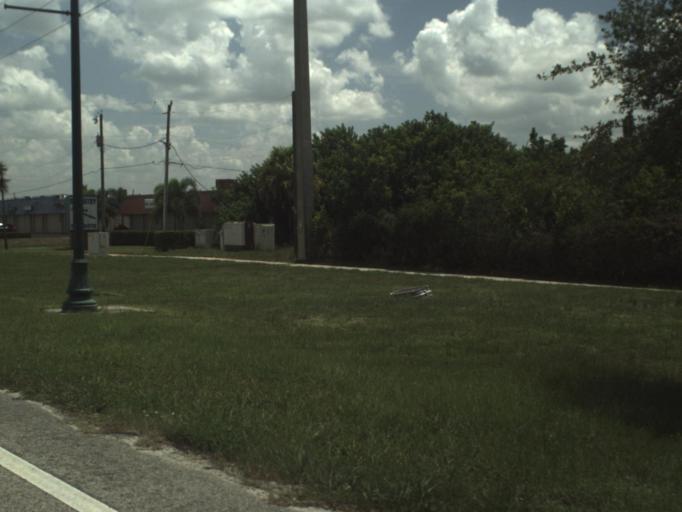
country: US
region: Florida
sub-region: Martin County
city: Hobe Sound
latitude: 27.0746
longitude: -80.1433
